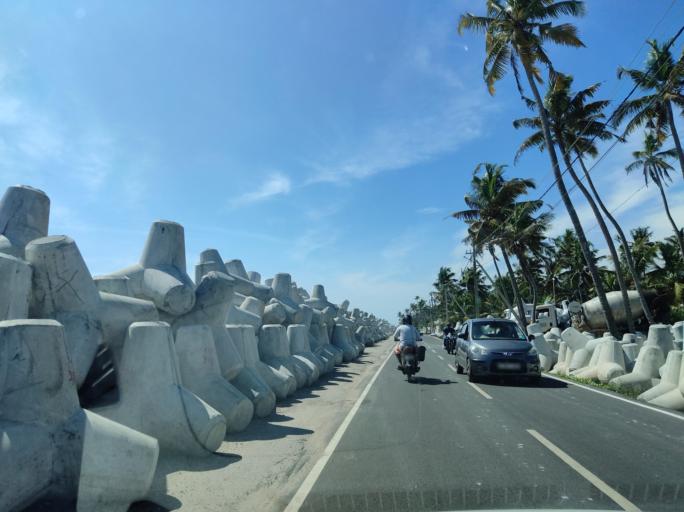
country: IN
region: Kerala
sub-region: Alappuzha
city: Kayankulam
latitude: 9.2110
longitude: 76.4293
